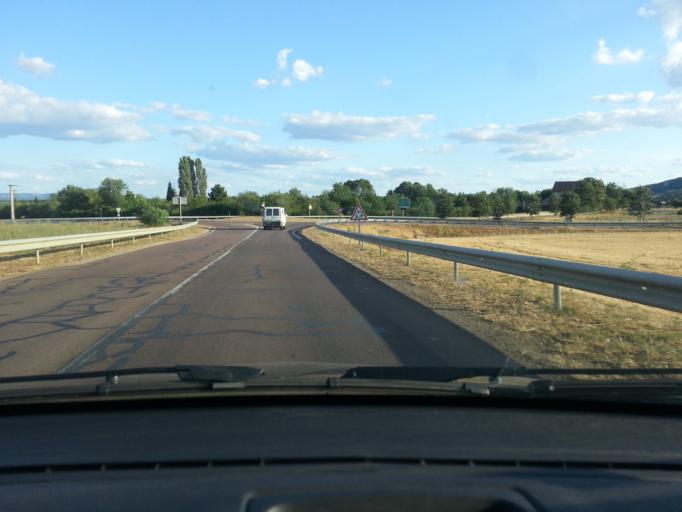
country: FR
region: Bourgogne
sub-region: Departement de Saone-et-Loire
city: Givry
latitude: 46.7571
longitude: 4.7219
